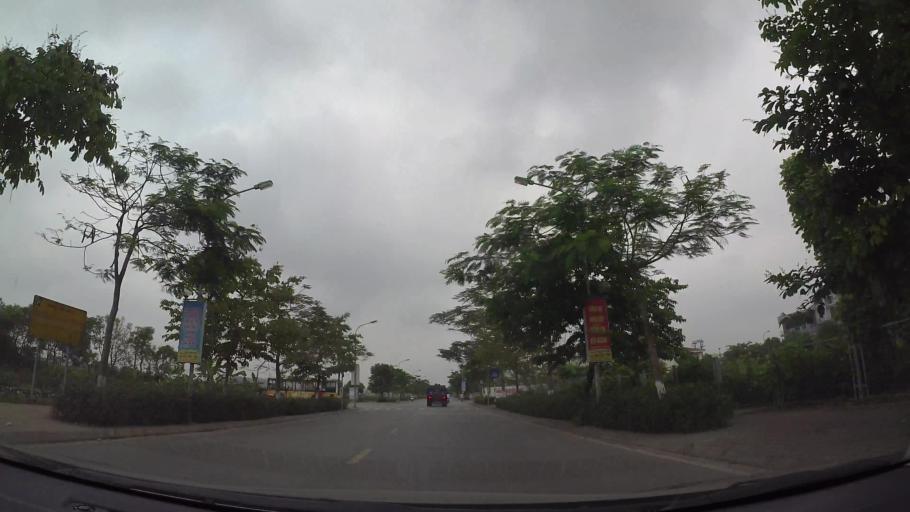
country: VN
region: Ha Noi
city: Trau Quy
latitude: 21.0452
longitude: 105.9244
